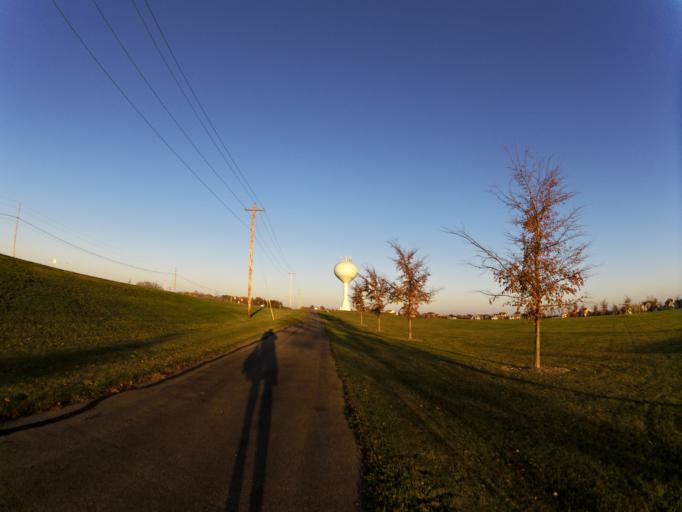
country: US
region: Minnesota
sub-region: Olmsted County
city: Rochester
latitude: 44.0477
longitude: -92.4173
